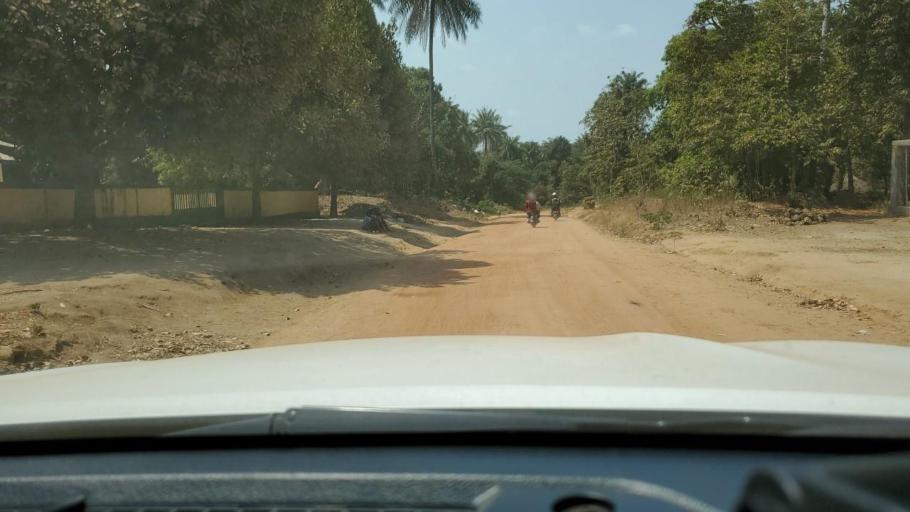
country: GN
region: Boke
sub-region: Boffa
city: Boffa
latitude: 10.0854
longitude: -13.8650
